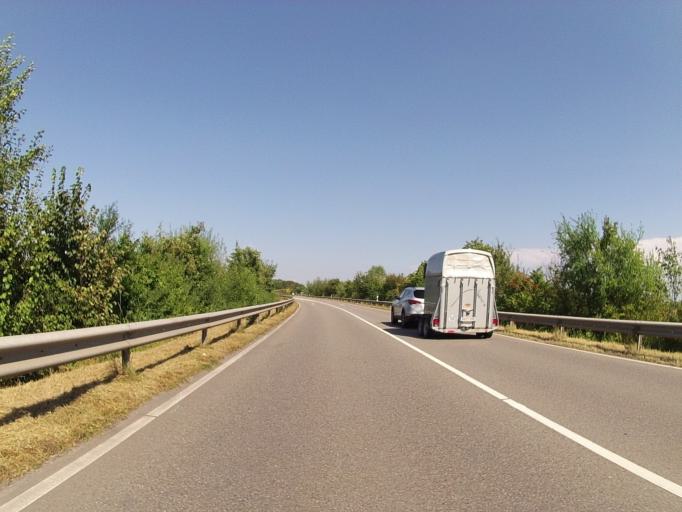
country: DE
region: Rheinland-Pfalz
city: Worth am Rhein
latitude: 49.0366
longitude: 8.2688
